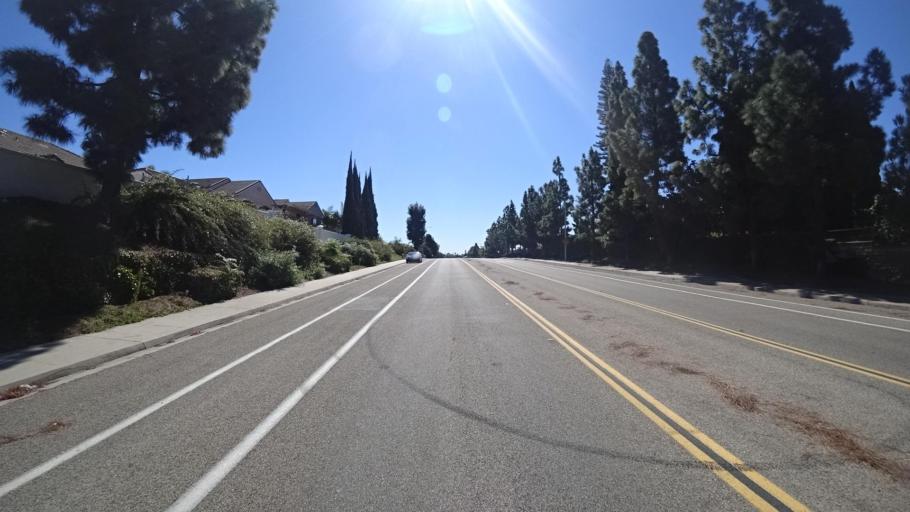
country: US
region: California
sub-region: San Diego County
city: Bonita
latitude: 32.6543
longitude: -116.9902
